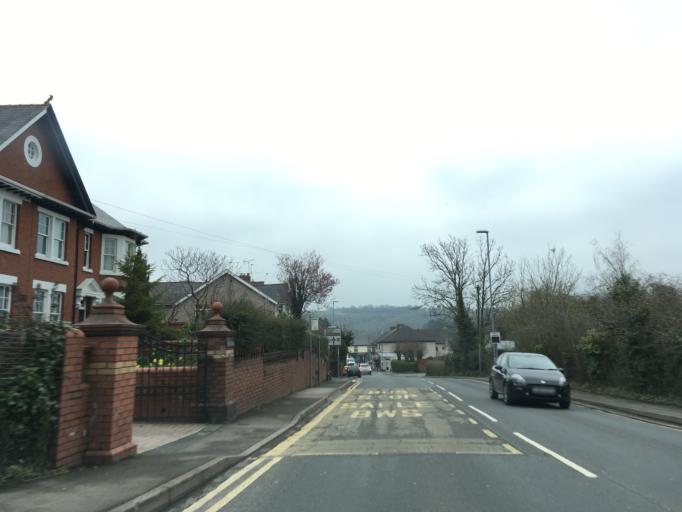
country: GB
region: Wales
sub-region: Newport
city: Caerleon
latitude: 51.6144
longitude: -2.9583
